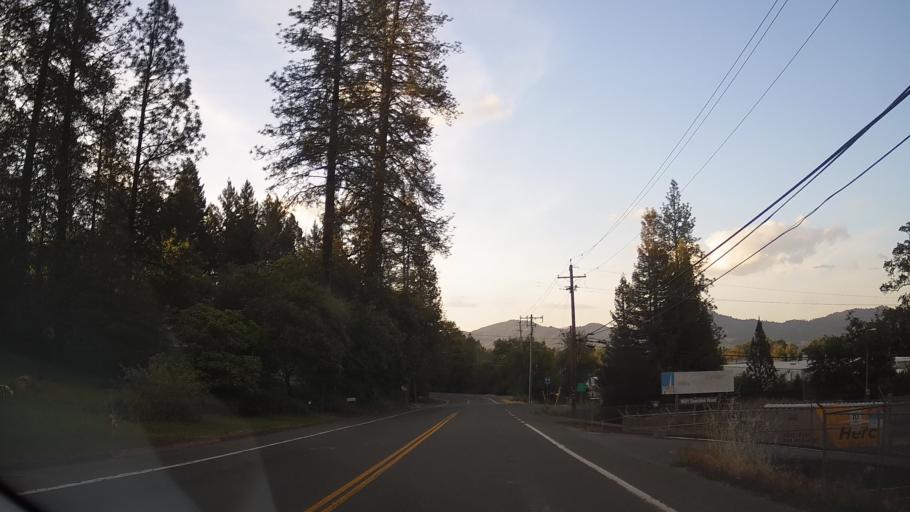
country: US
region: California
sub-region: Mendocino County
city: Willits
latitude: 39.3907
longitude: -123.3436
